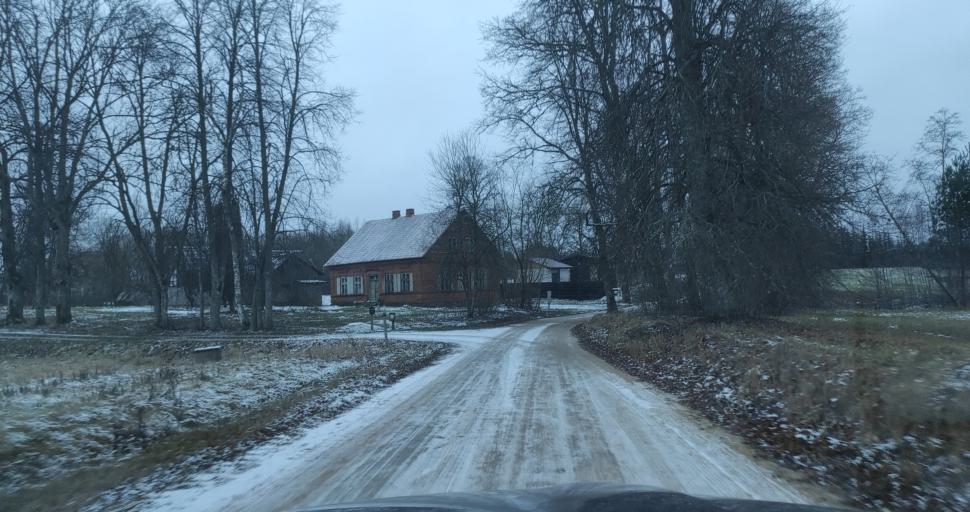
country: LV
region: Kuldigas Rajons
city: Kuldiga
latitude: 56.9783
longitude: 22.0530
